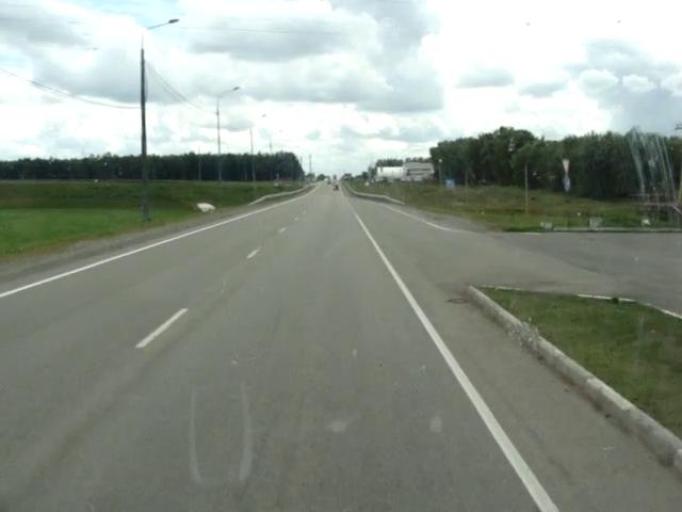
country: RU
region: Altai Krai
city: Zarya
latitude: 52.5789
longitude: 85.1772
